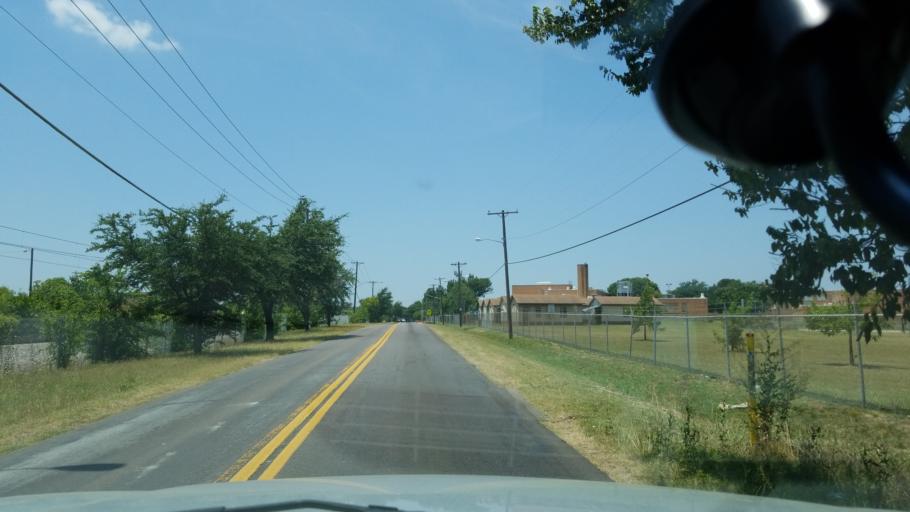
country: US
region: Texas
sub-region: Dallas County
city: Cockrell Hill
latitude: 32.7215
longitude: -96.8673
